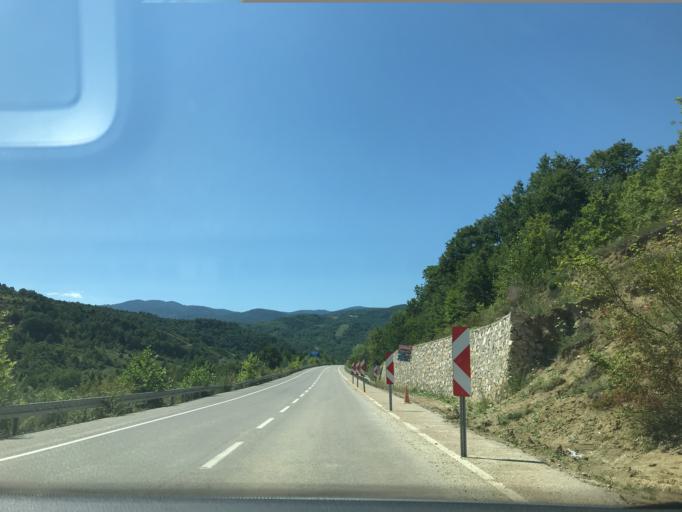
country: TR
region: Bursa
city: Tahtakopru
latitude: 39.9701
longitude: 29.6048
